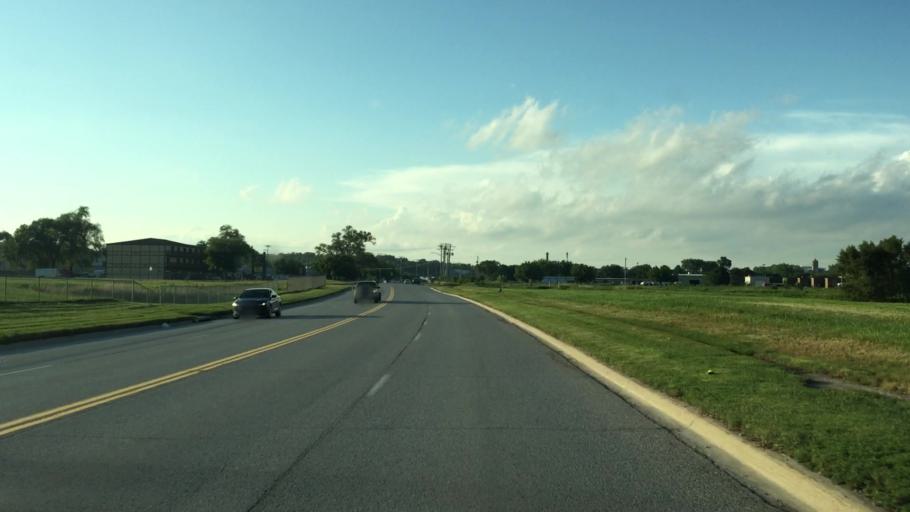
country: US
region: Iowa
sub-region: Johnson County
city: Iowa City
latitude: 41.6426
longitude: -91.5393
